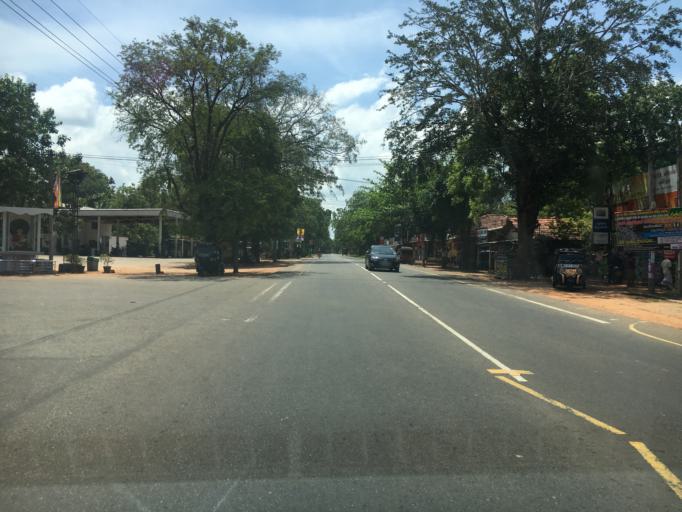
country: LK
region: North Central
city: Anuradhapura
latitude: 8.2698
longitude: 80.5024
